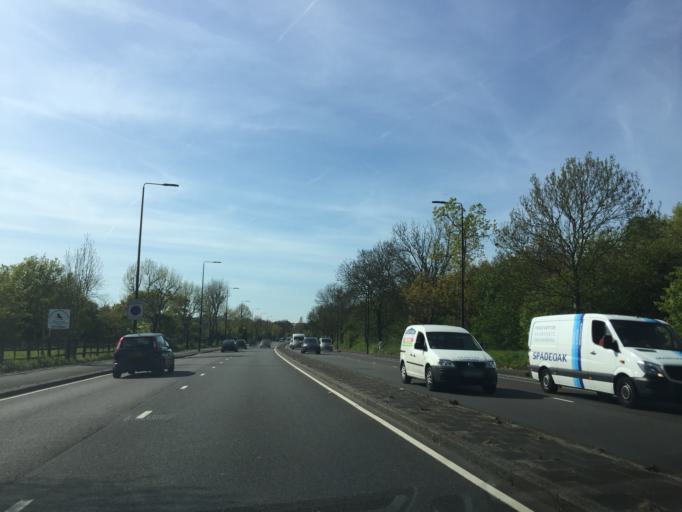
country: GB
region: England
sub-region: Greater London
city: Blackheath
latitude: 51.4419
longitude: 0.0382
